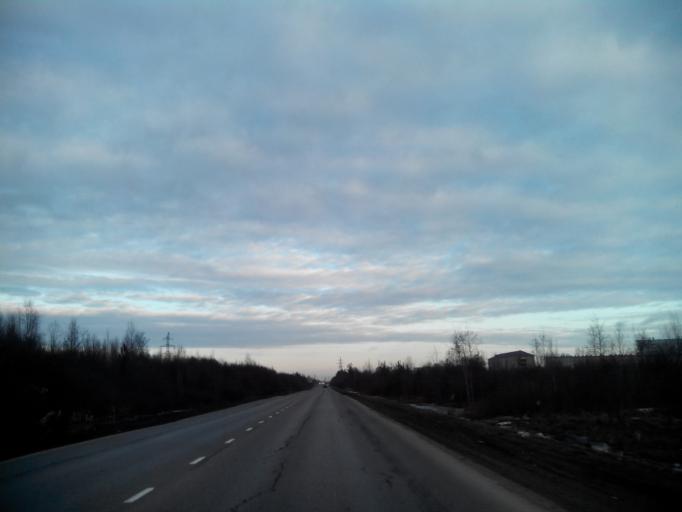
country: RU
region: Arkhangelskaya
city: Arkhangel'sk
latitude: 64.5247
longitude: 40.6649
